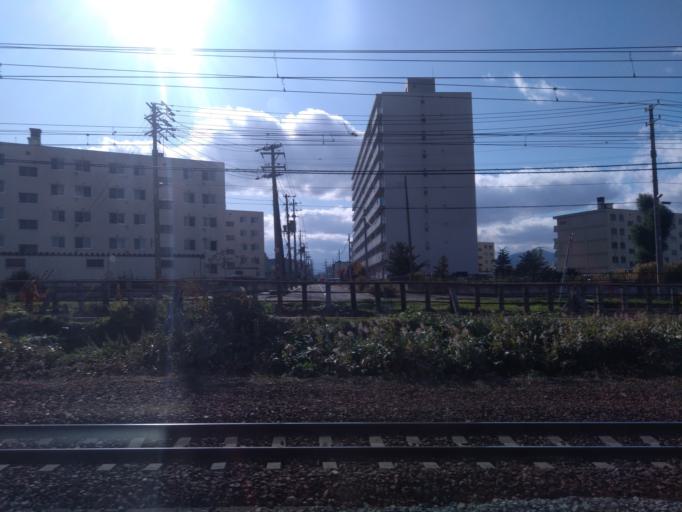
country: JP
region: Hokkaido
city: Sapporo
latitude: 43.0581
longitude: 141.4084
